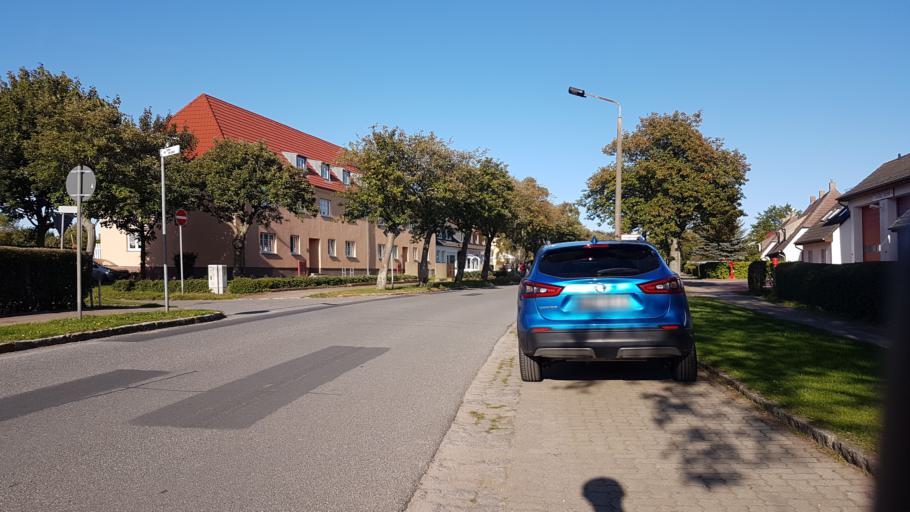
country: DE
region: Mecklenburg-Vorpommern
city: Dranske
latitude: 54.6282
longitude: 13.2288
